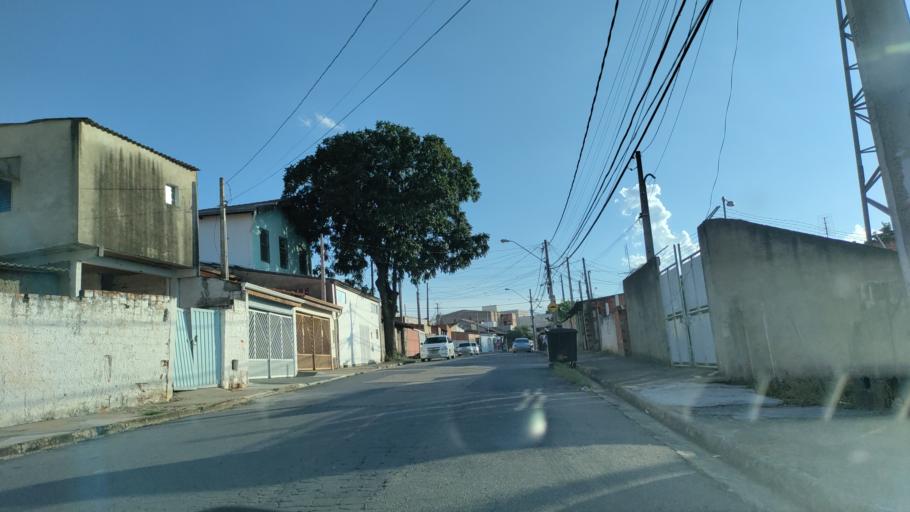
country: BR
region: Sao Paulo
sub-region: Sorocaba
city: Sorocaba
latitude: -23.4746
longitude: -47.4663
